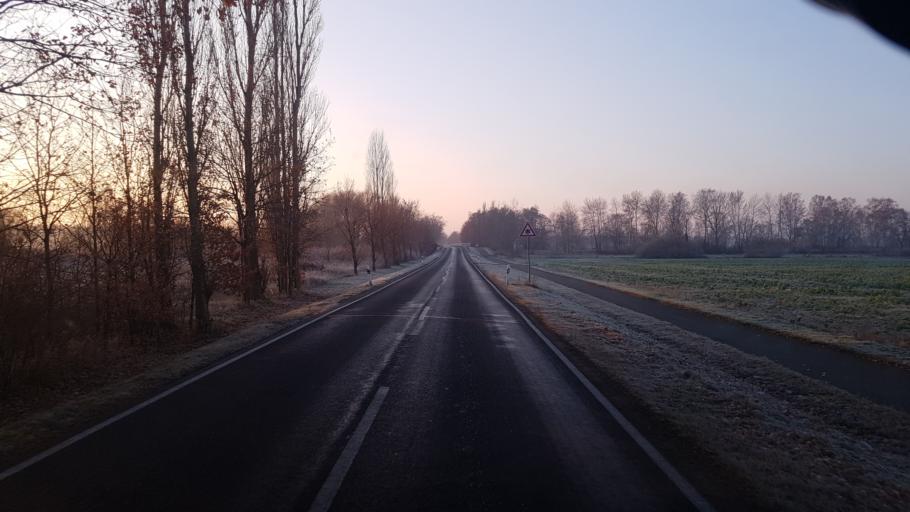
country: DE
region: Brandenburg
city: Tettau
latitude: 51.4622
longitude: 13.7398
